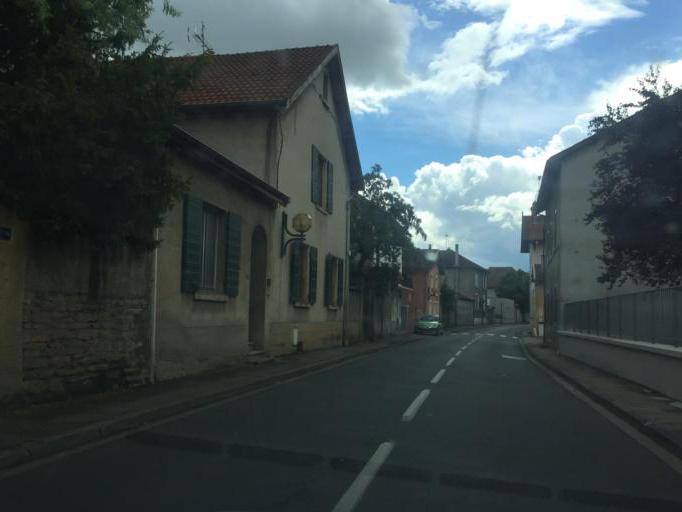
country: FR
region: Rhone-Alpes
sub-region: Departement de l'Isere
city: Pont-de-Cheruy
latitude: 45.7514
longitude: 5.1783
